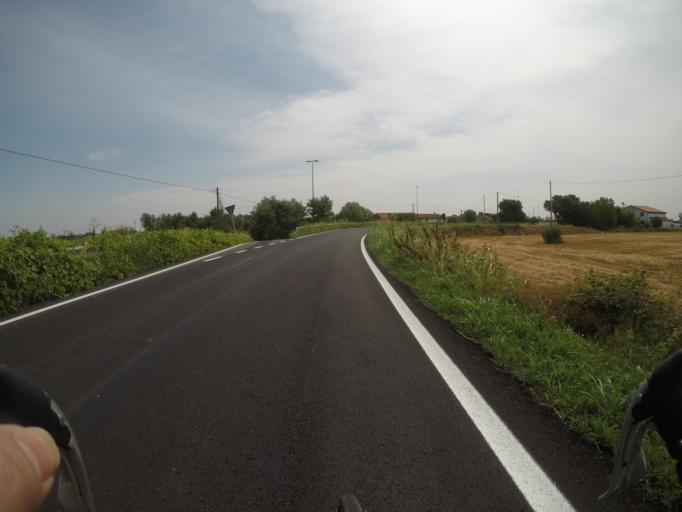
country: IT
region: Veneto
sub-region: Provincia di Rovigo
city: Villanova del Ghebbo Canton
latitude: 45.0524
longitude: 11.6542
